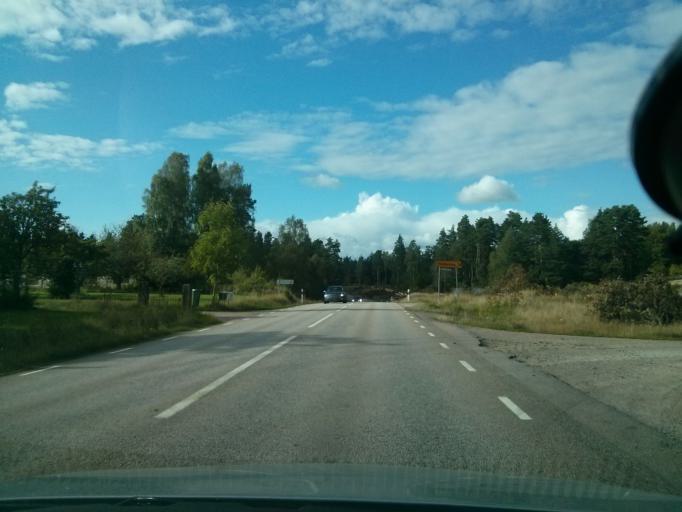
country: SE
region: Blekinge
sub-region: Ronneby Kommun
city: Brakne-Hoby
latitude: 56.3078
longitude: 15.1872
